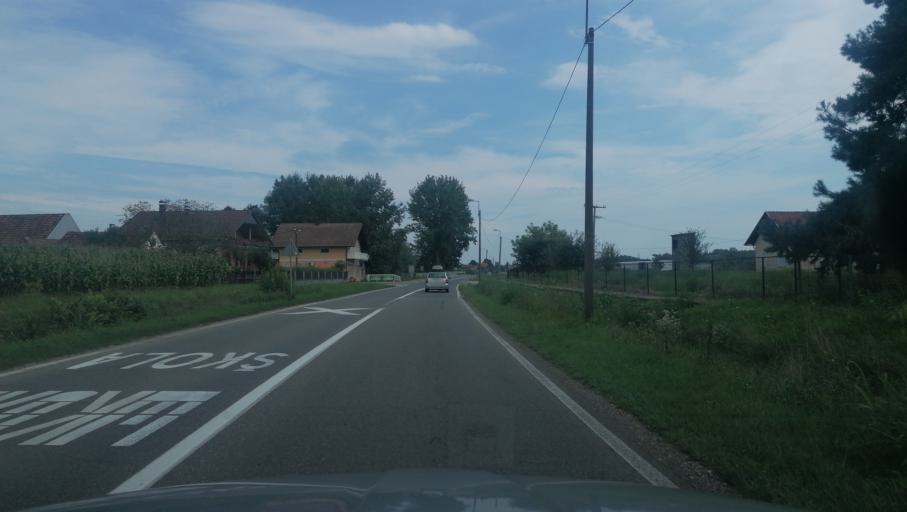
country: BA
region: Brcko
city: Brka
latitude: 44.9281
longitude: 18.7171
